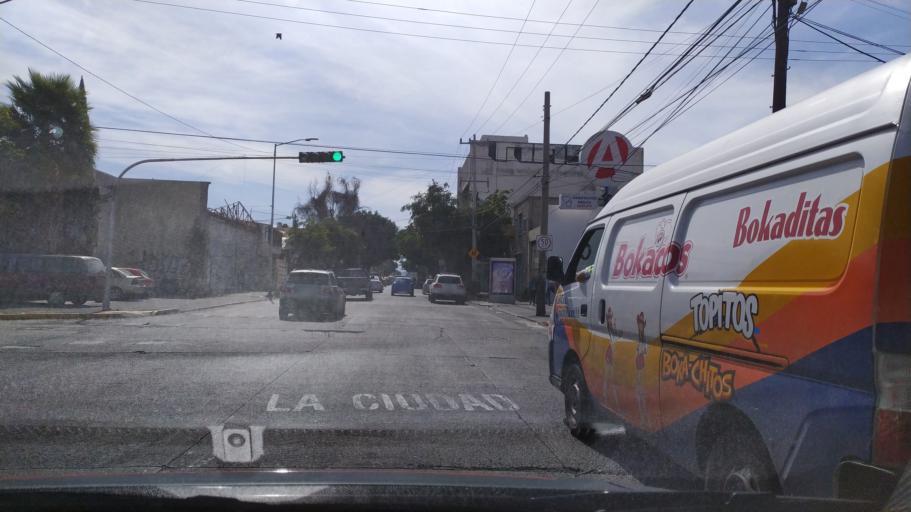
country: MX
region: Jalisco
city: Tlaquepaque
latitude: 20.6742
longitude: -103.3300
